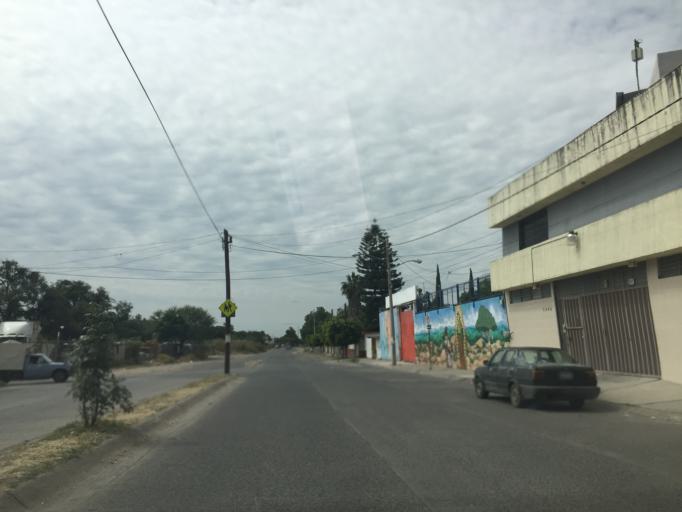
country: MX
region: Guanajuato
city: Leon
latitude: 21.1033
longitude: -101.7022
